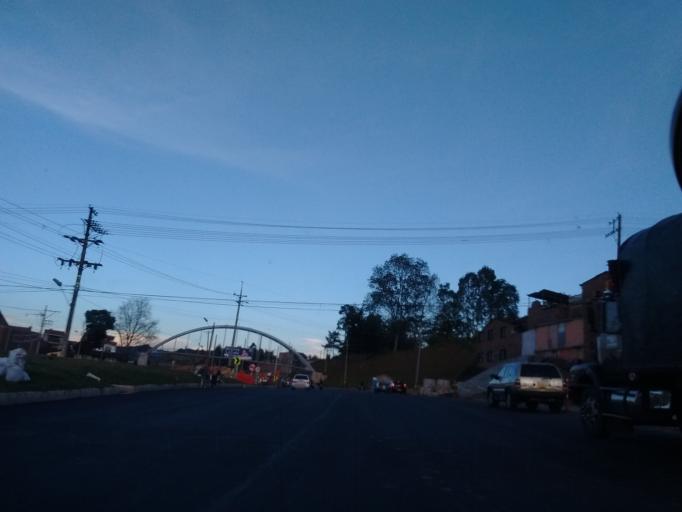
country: CO
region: Antioquia
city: Marinilla
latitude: 6.1683
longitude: -75.3384
